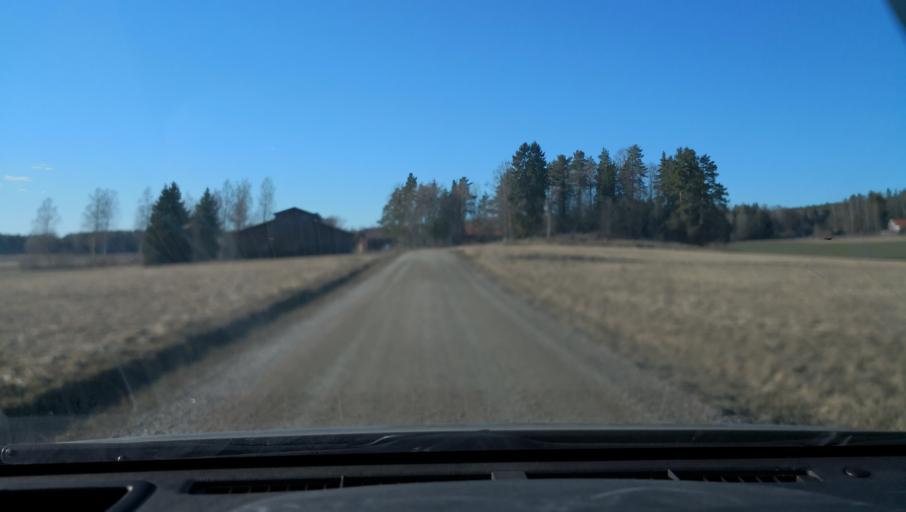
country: SE
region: Vaestmanland
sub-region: Sala Kommun
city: Sala
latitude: 60.1502
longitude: 16.6390
